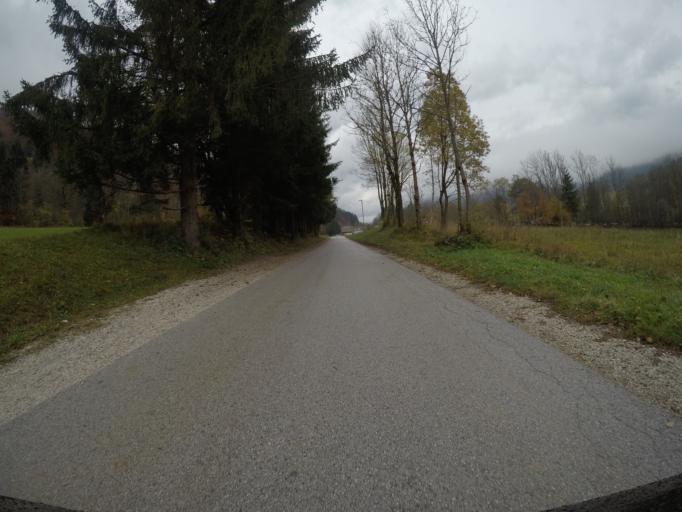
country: SI
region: Kranjska Gora
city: Kranjska Gora
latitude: 46.4894
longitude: 13.7687
